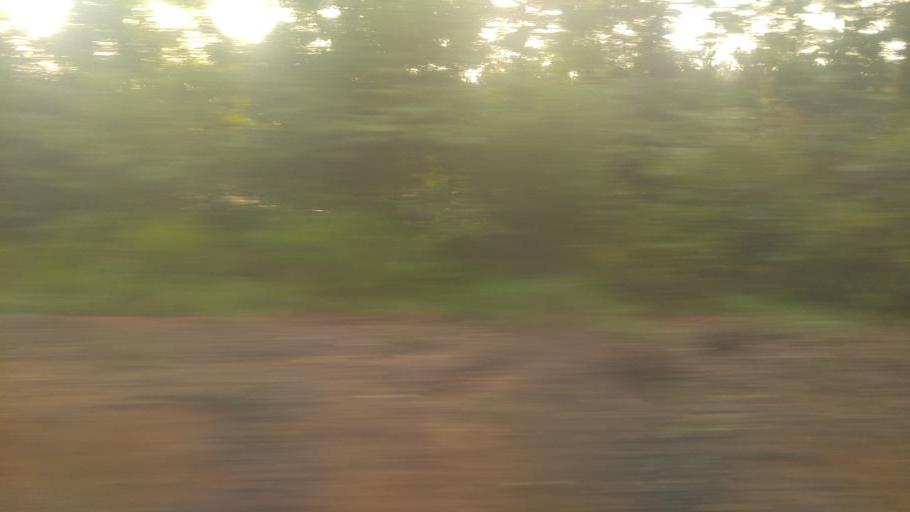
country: US
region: North Carolina
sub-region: Wake County
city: Raleigh
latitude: 35.7409
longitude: -78.6380
